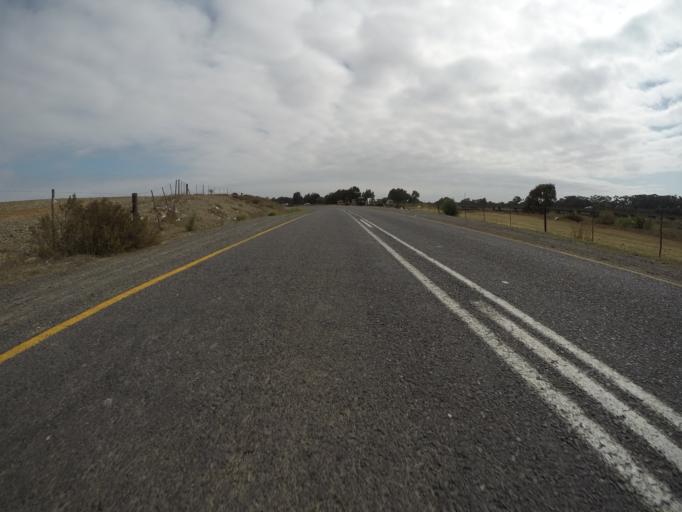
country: ZA
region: Western Cape
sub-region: City of Cape Town
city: Sunset Beach
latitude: -33.7907
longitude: 18.5506
